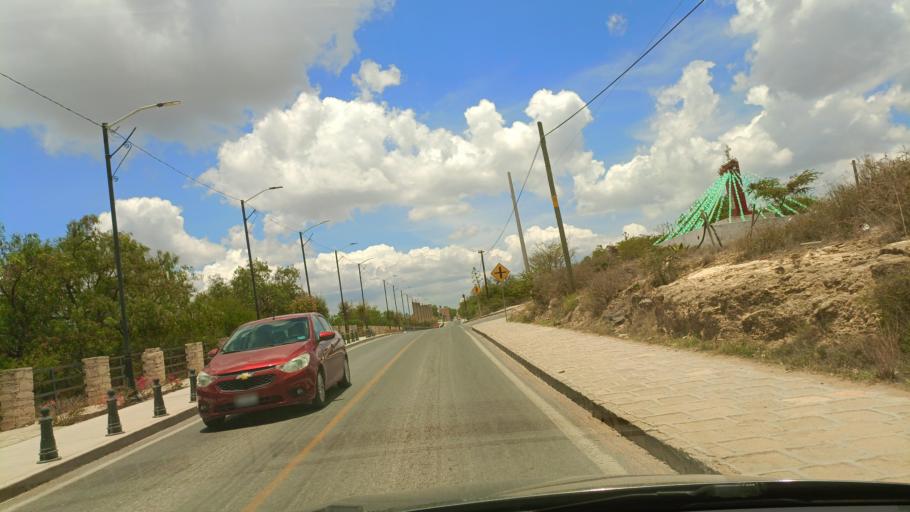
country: MX
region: Guanajuato
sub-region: San Luis de la Paz
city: San Ignacio
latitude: 21.2291
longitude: -100.4913
